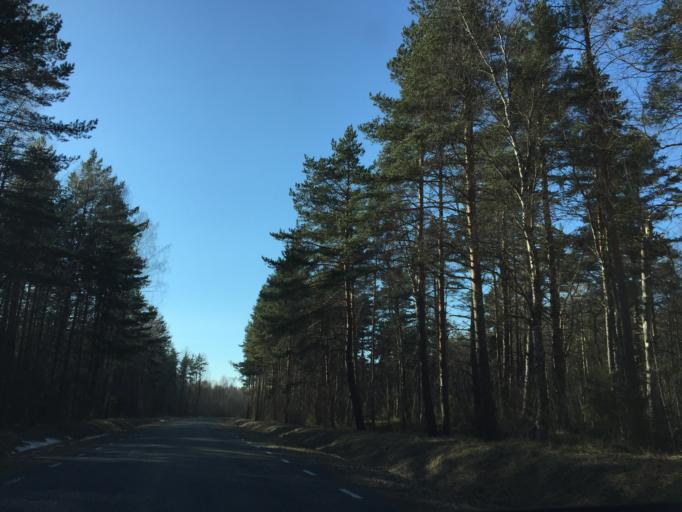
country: RU
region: Pskov
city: Gdov
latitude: 58.9997
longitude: 27.7002
